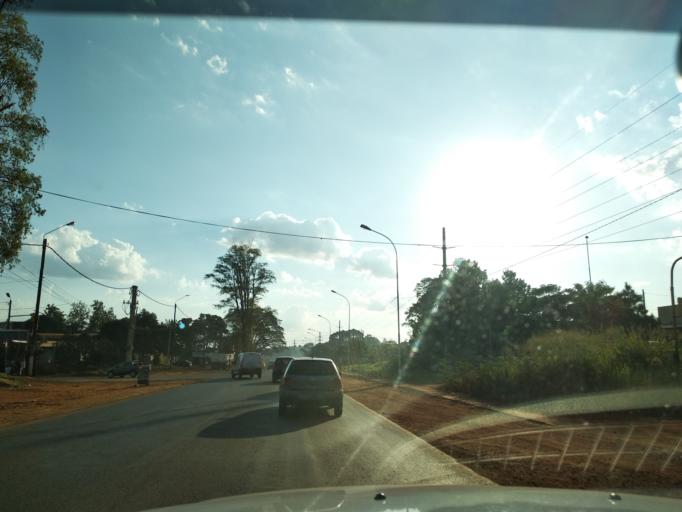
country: AR
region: Misiones
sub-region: Departamento de Capital
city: Posadas
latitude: -27.4287
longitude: -55.9375
